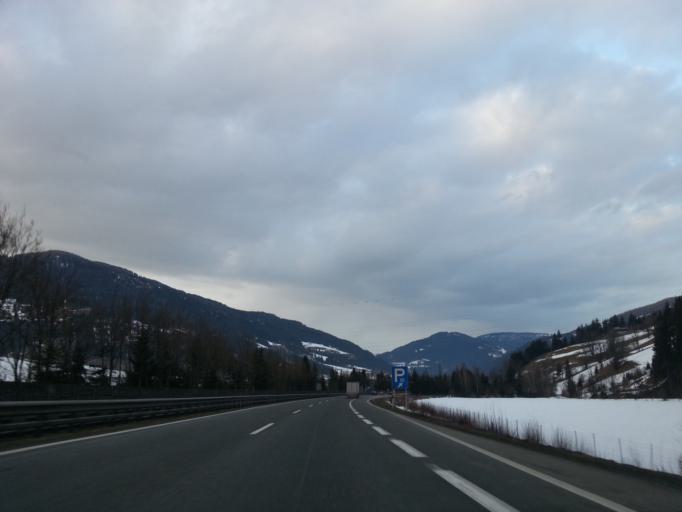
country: AT
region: Salzburg
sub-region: Politischer Bezirk Sankt Johann im Pongau
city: Flachau
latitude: 47.3682
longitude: 13.3950
